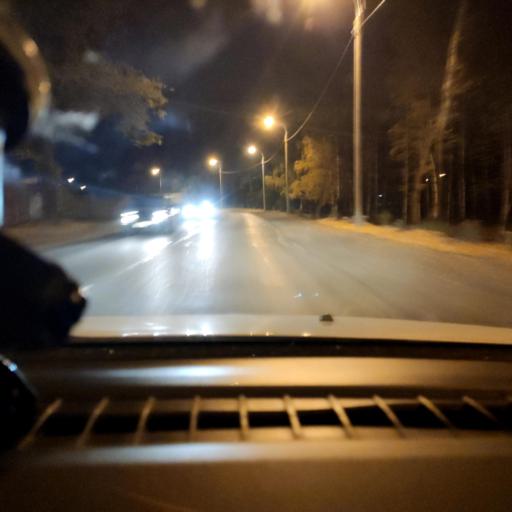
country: RU
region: Samara
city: Rozhdestveno
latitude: 53.1438
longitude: 50.0356
